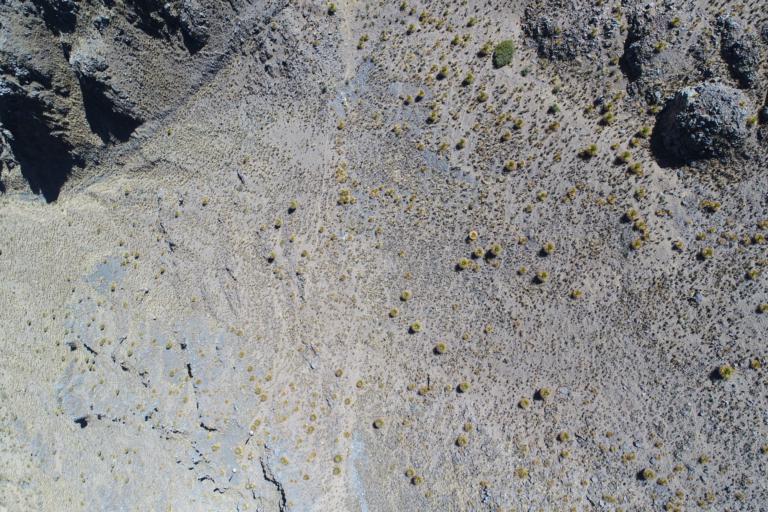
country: BO
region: La Paz
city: Viloco
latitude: -16.8065
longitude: -67.5470
